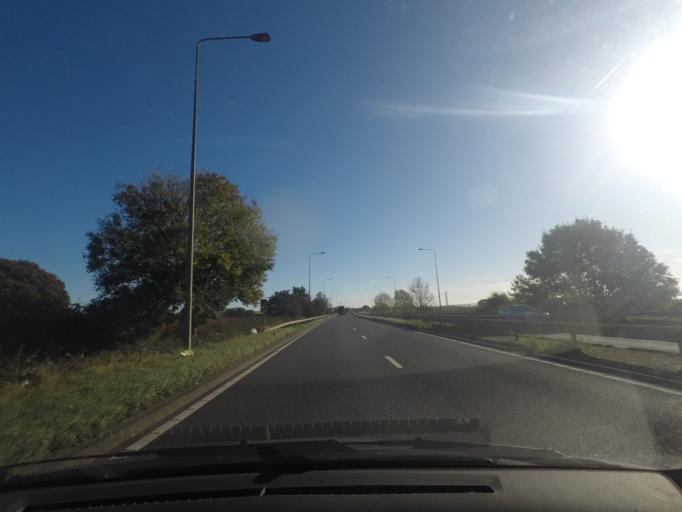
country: GB
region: England
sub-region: East Riding of Yorkshire
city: North Ferriby
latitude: 53.7262
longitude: -0.4953
